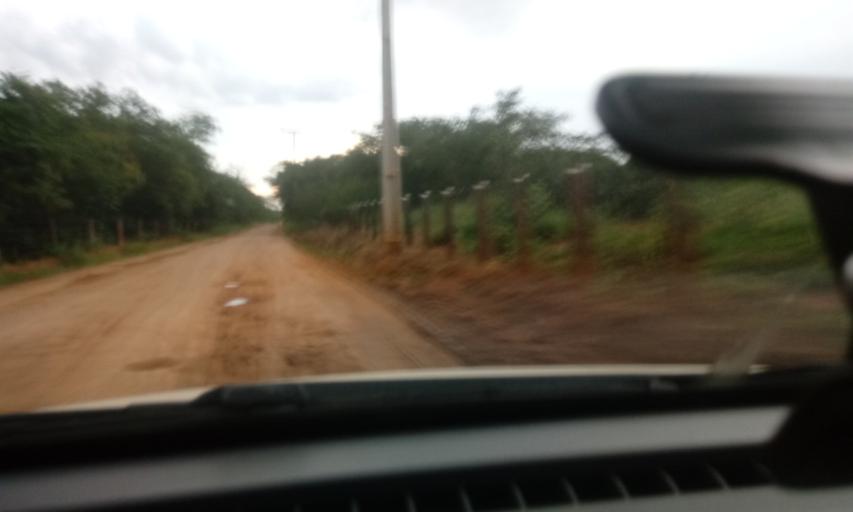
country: BR
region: Bahia
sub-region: Riacho De Santana
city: Riacho de Santana
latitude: -13.7911
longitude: -42.7303
